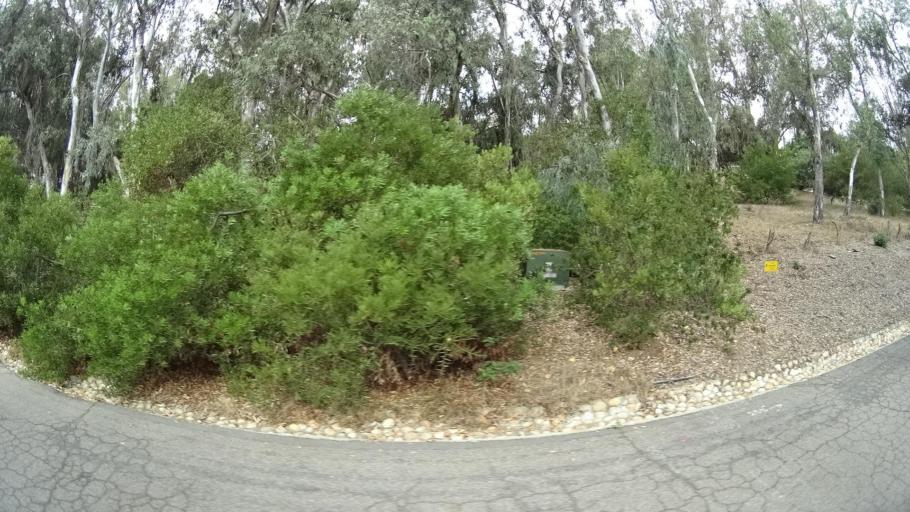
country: US
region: California
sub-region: San Diego County
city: Rancho Santa Fe
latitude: 33.0046
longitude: -117.2327
